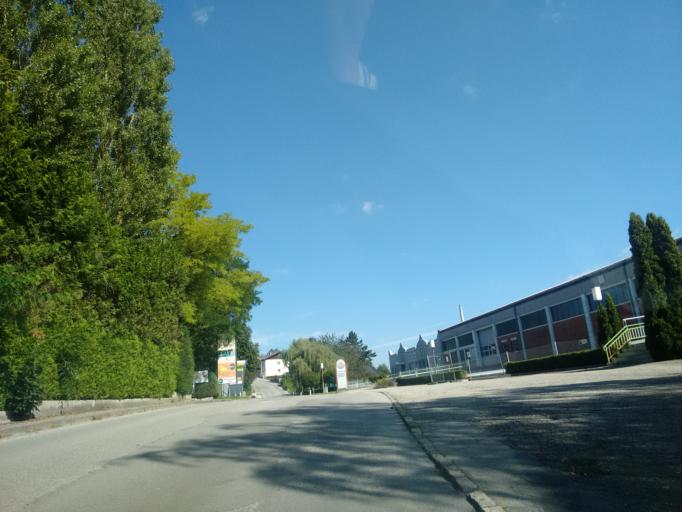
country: AT
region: Upper Austria
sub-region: Politischer Bezirk Steyr-Land
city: Pfarrkirchen bei Bad Hall
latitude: 48.0253
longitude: 14.2047
